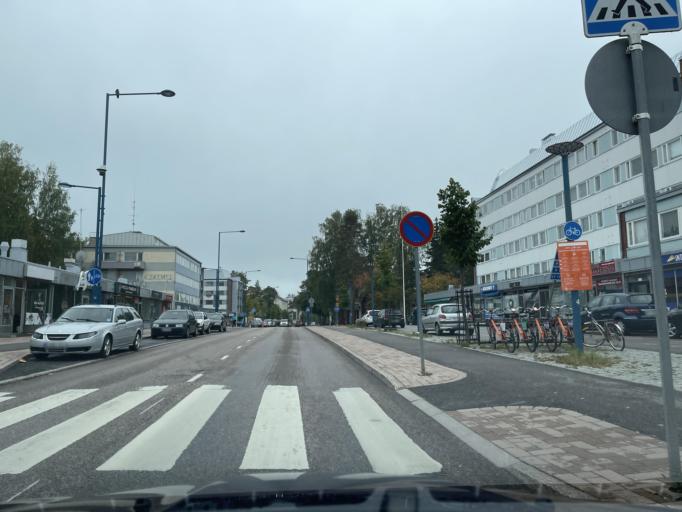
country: FI
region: Uusimaa
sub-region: Helsinki
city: Hyvinge
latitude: 60.6289
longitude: 24.8571
